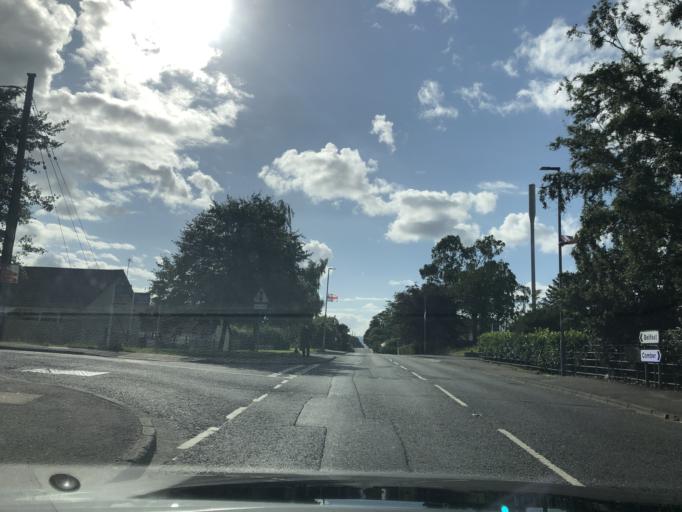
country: GB
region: Northern Ireland
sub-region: Castlereagh District
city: Dundonald
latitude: 54.5864
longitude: -5.8055
